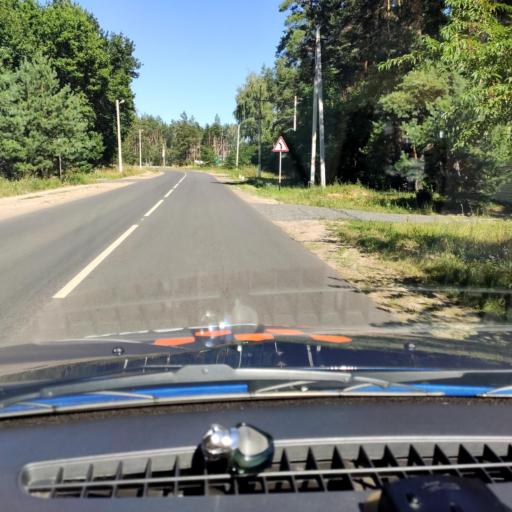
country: RU
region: Voronezj
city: Podgornoye
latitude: 51.7851
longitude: 39.1445
